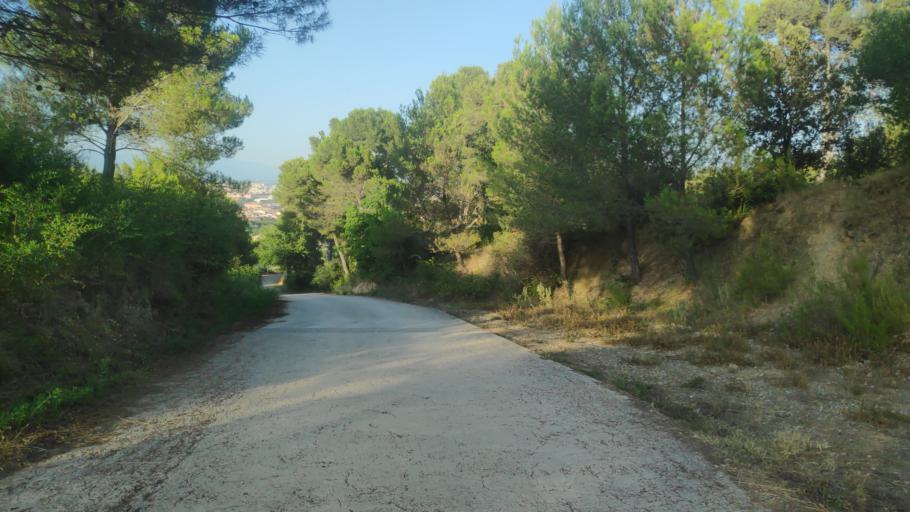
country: ES
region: Catalonia
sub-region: Provincia de Barcelona
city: Sant Quirze del Valles
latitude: 41.5222
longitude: 2.0692
